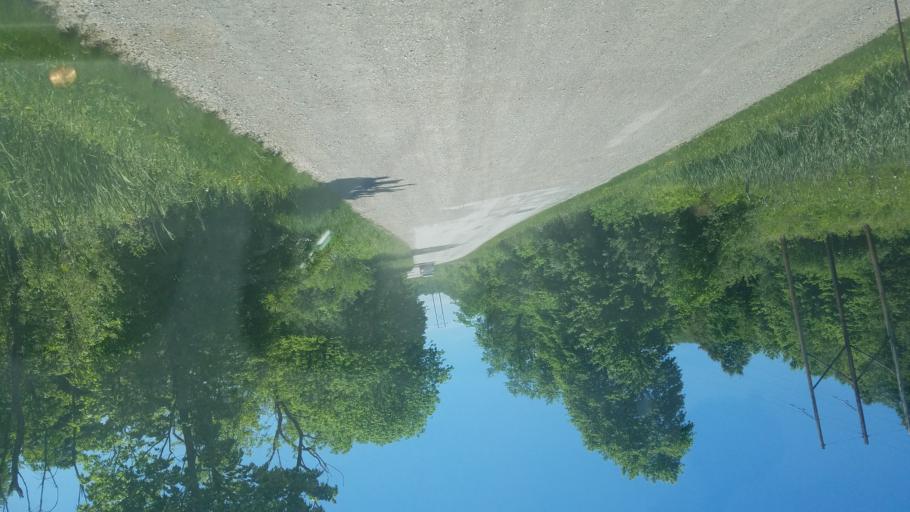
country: US
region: Ohio
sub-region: Coshocton County
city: Coshocton
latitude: 40.2731
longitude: -81.9700
